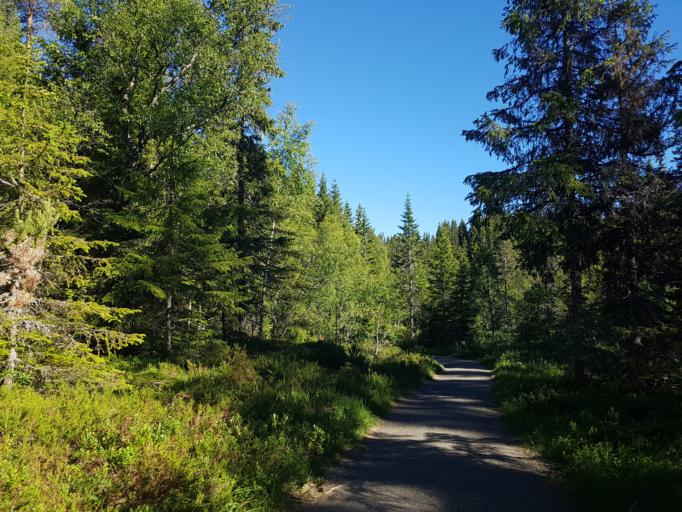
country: NO
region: Sor-Trondelag
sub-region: Trondheim
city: Trondheim
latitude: 63.4228
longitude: 10.2921
